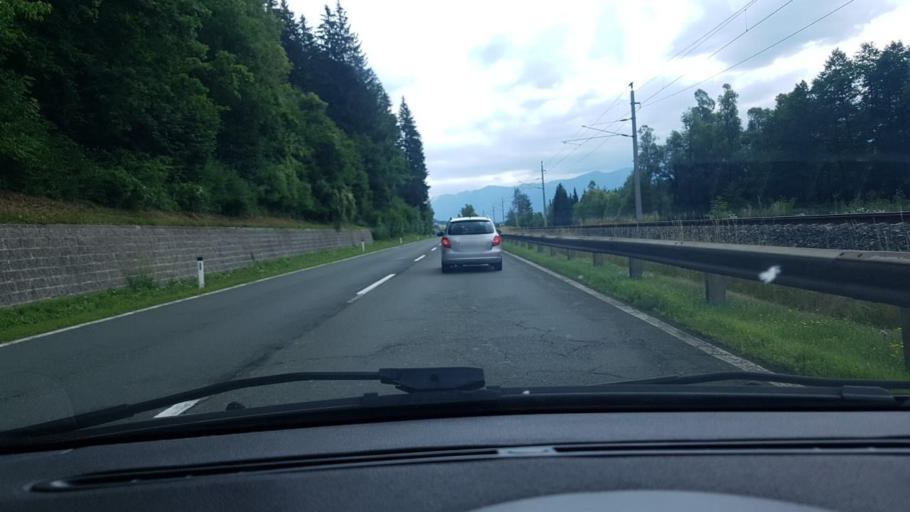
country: AT
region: Carinthia
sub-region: Politischer Bezirk Villach Land
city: Feistritz an der Gail
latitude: 46.5960
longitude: 13.5953
